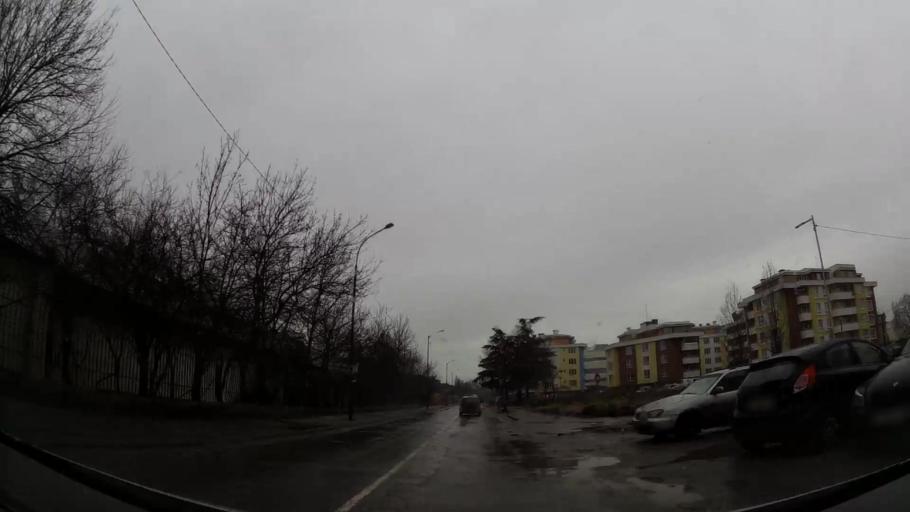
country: BG
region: Sofia-Capital
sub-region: Stolichna Obshtina
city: Sofia
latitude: 42.6644
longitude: 23.4060
